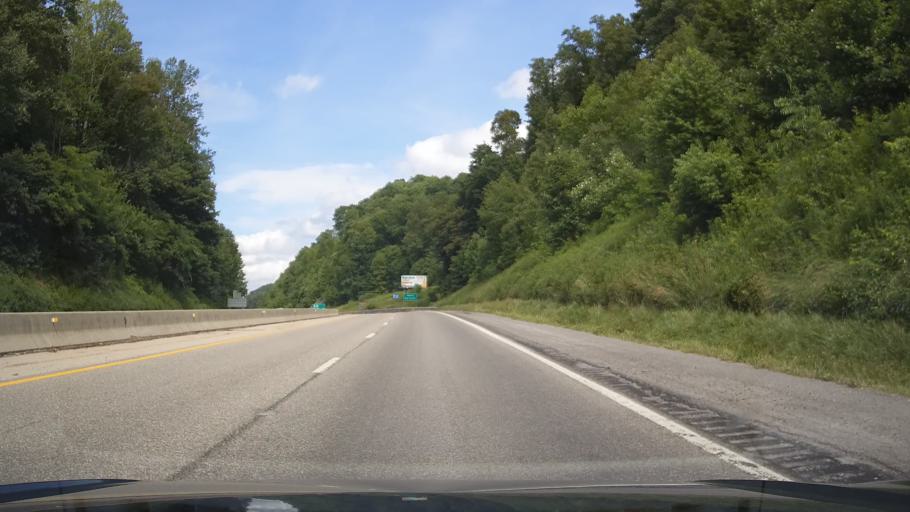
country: US
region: Virginia
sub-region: City of Norton
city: Norton
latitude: 36.9269
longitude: -82.6442
